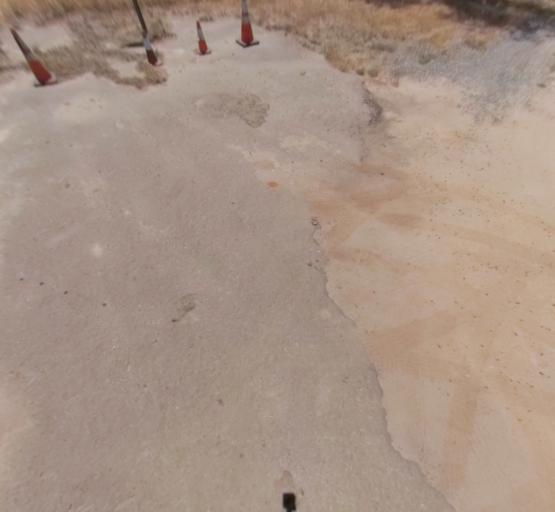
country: US
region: California
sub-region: Madera County
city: Madera Acres
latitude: 36.9929
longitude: -120.0915
